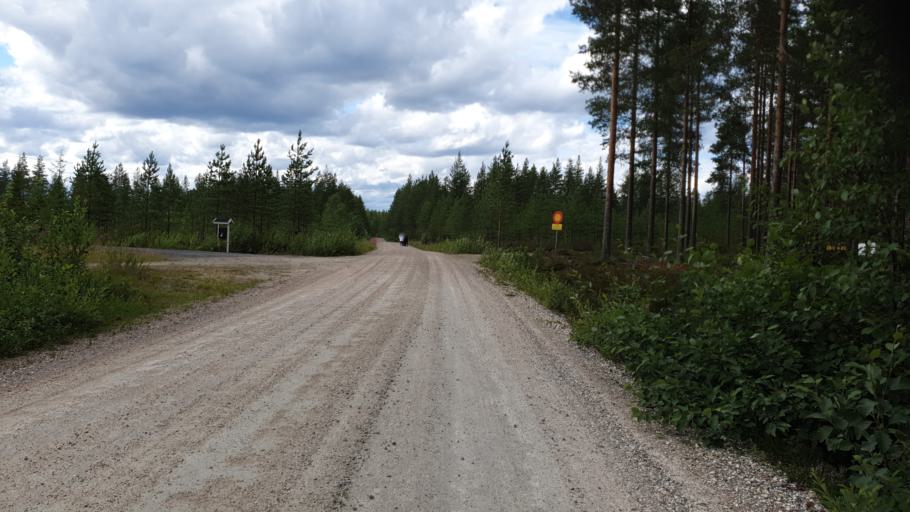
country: FI
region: Kainuu
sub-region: Kehys-Kainuu
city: Kuhmo
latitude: 64.3837
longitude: 29.7970
